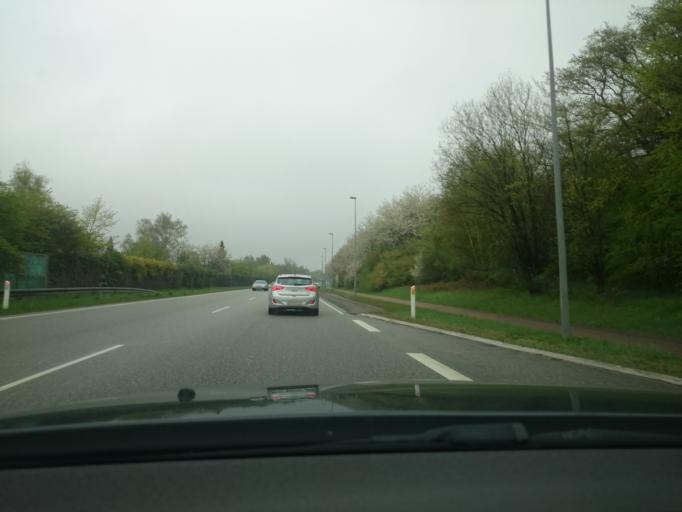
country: DK
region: Capital Region
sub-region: Ballerup Kommune
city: Ballerup
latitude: 55.7387
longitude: 12.3807
